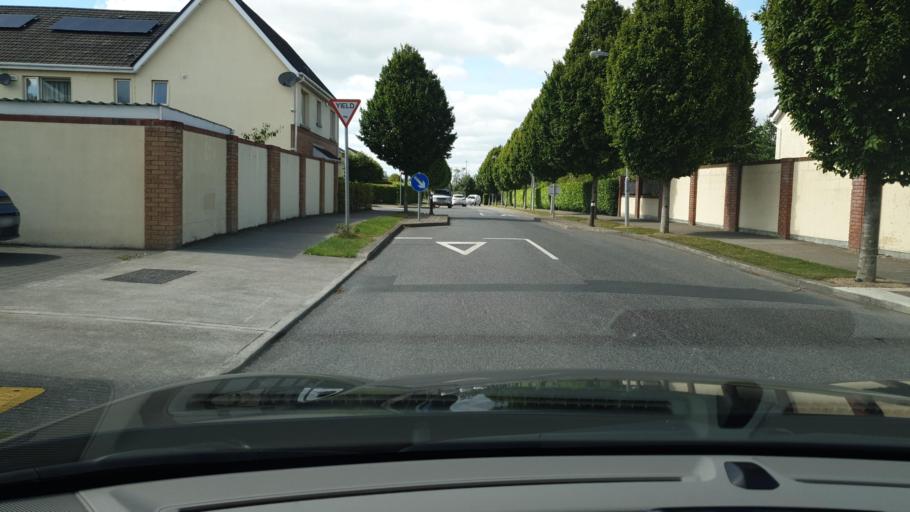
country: IE
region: Leinster
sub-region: An Mhi
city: Dunboyne
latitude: 53.4144
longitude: -6.4818
